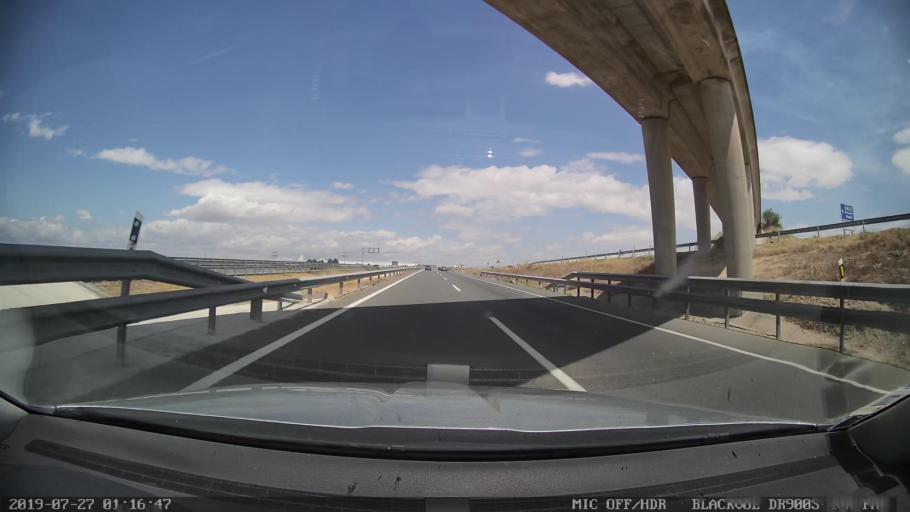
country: ES
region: Castille-La Mancha
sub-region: Province of Toledo
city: Maqueda
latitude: 40.0680
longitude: -4.3656
